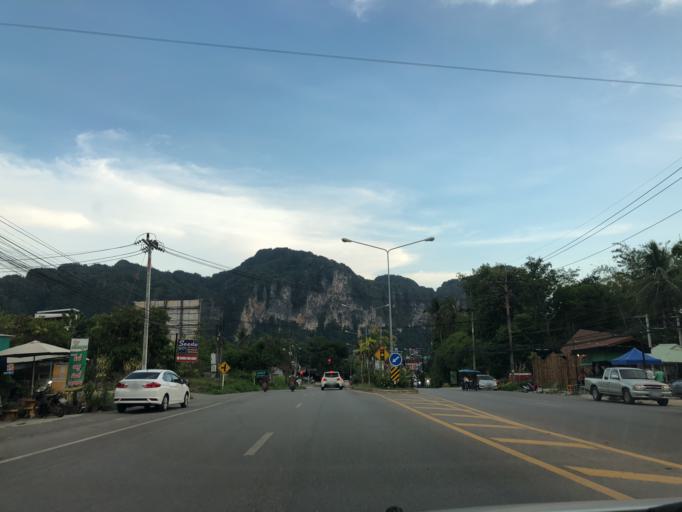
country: TH
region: Phangnga
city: Ban Ao Nang
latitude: 8.0429
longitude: 98.8369
